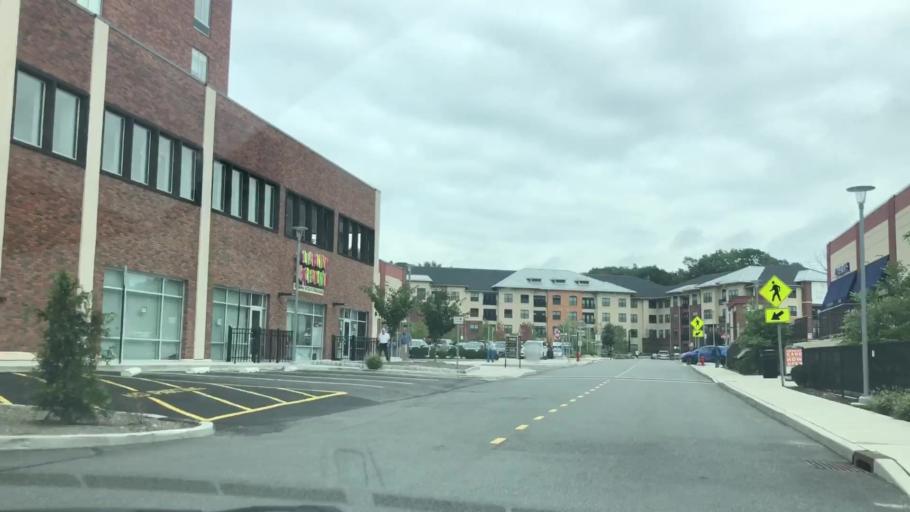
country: US
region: New York
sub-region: Westchester County
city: Ardsley
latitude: 41.0037
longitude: -73.8572
